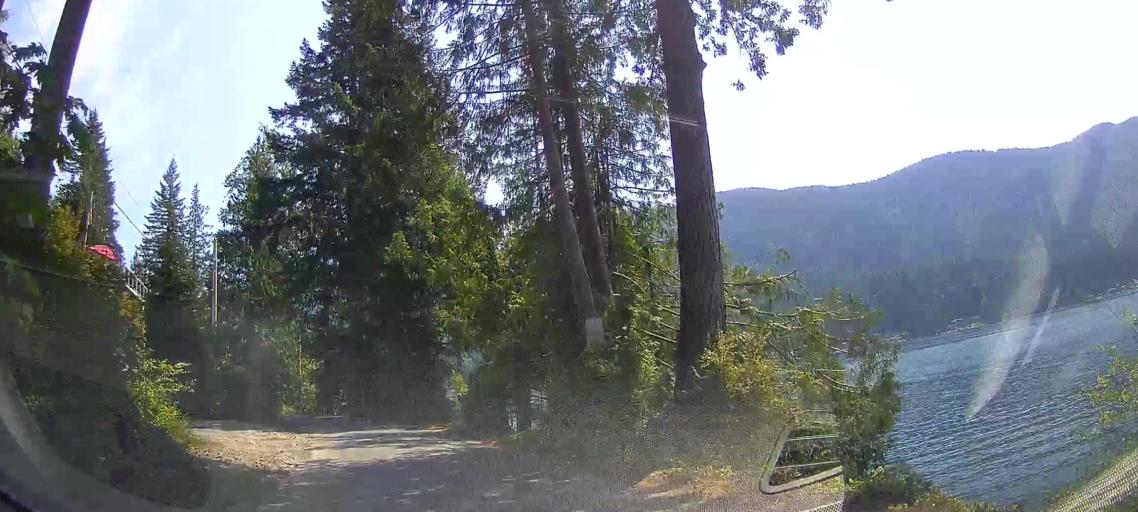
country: US
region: Washington
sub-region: Snohomish County
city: Arlington Heights
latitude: 48.3243
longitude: -122.0071
